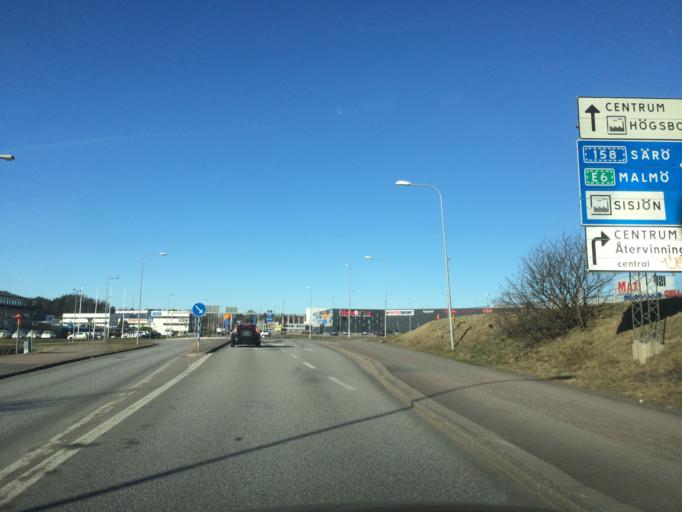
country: SE
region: Vaestra Goetaland
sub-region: Goteborg
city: Majorna
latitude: 57.6499
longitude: 11.9536
